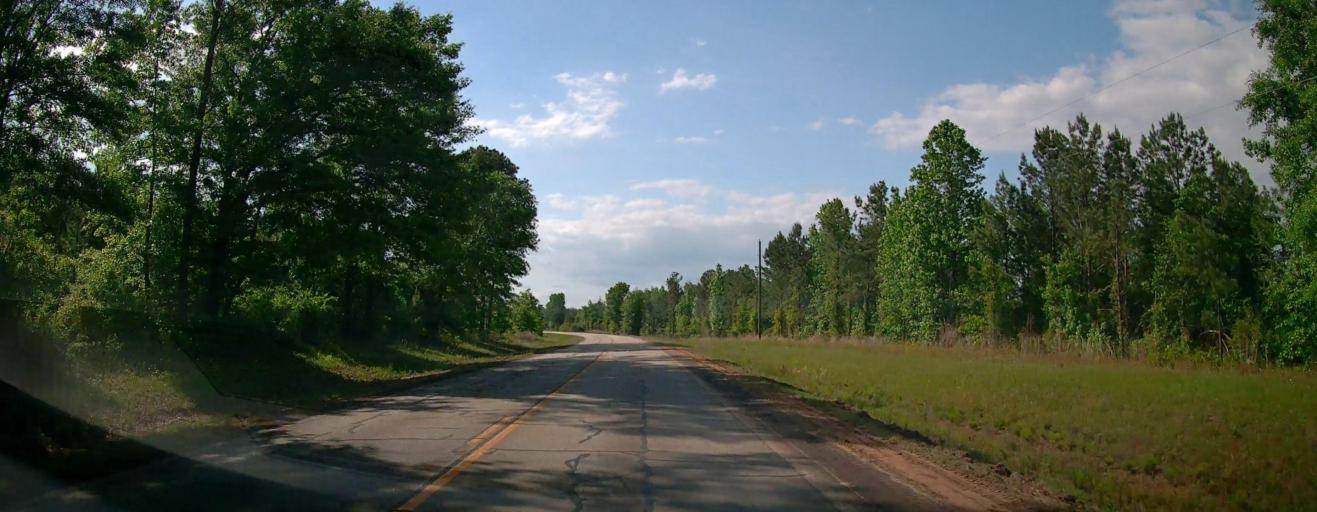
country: US
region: Georgia
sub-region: Washington County
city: Tennille
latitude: 32.9140
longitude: -82.9879
